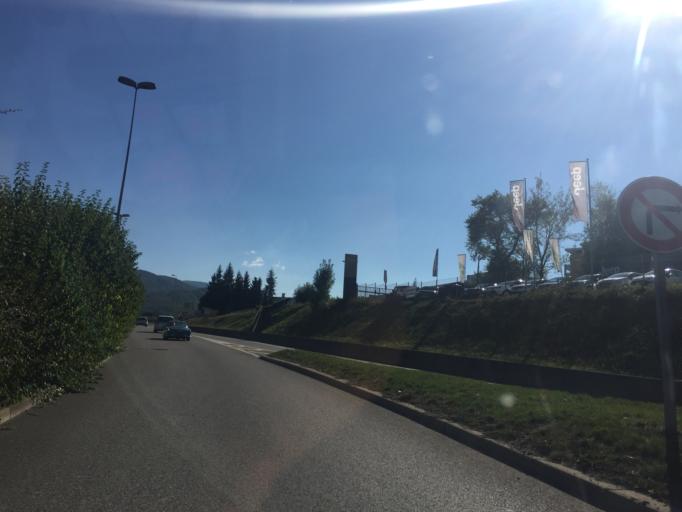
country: FR
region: Rhone-Alpes
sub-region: Departement de la Haute-Savoie
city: Annecy
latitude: 45.8955
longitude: 6.1111
